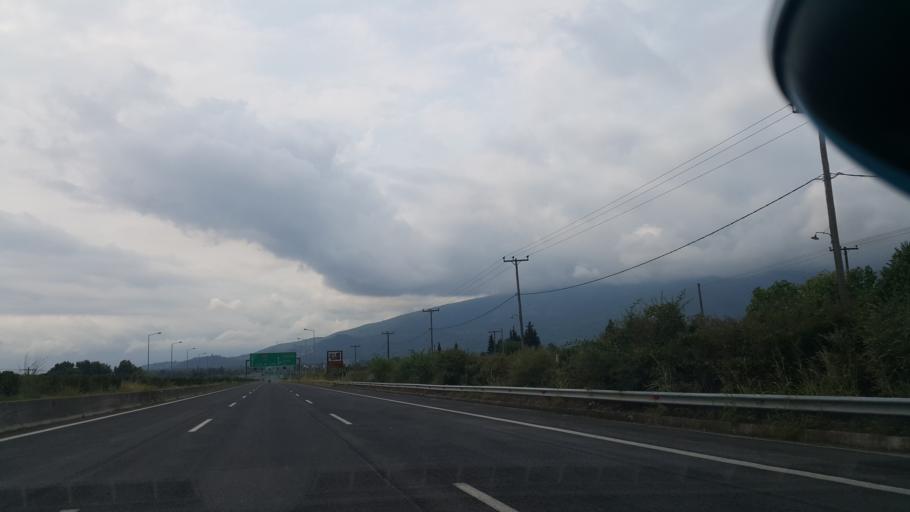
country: GR
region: Central Macedonia
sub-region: Nomos Pierias
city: Leptokarya
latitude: 40.0528
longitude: 22.5596
